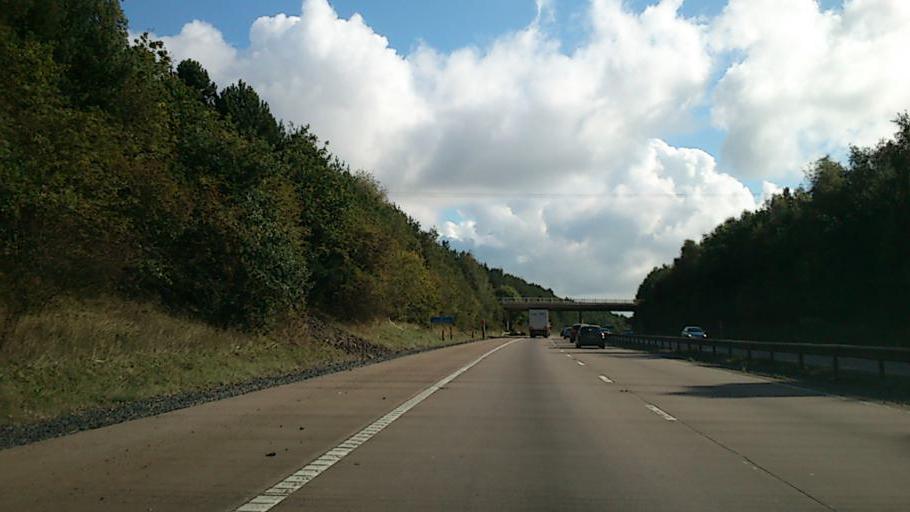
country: GB
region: England
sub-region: Shropshire
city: Albrighton
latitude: 52.6491
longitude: -2.2369
